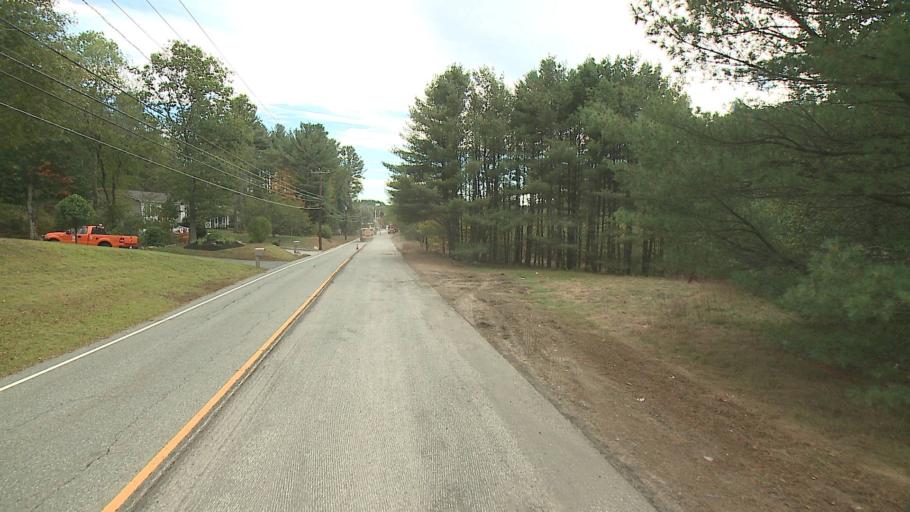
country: US
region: Connecticut
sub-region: Windham County
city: Killingly Center
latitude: 41.8453
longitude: -71.8776
